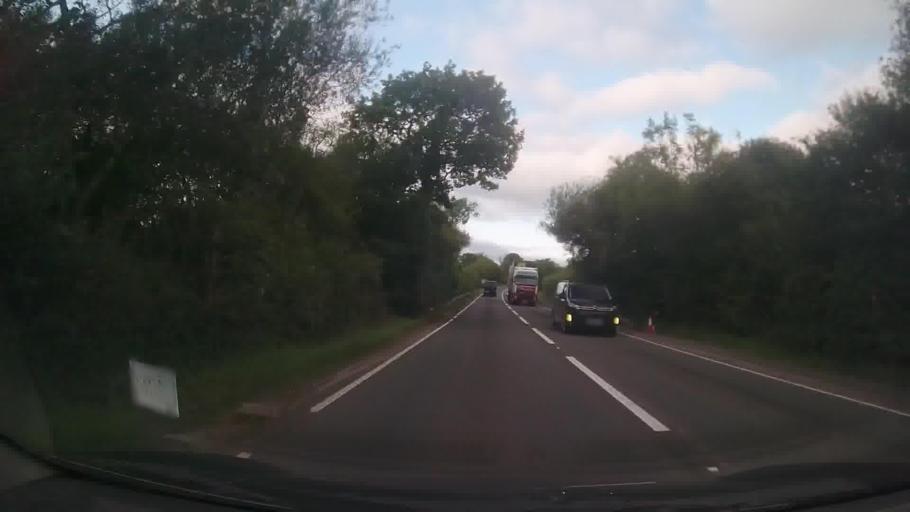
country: GB
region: Wales
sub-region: Pembrokeshire
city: Jeffreyston
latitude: 51.7243
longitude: -4.7467
